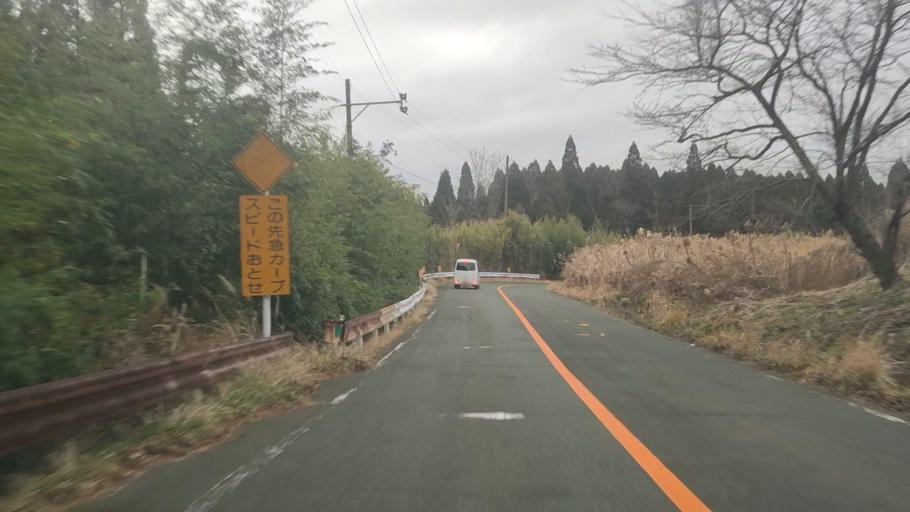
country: JP
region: Kumamoto
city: Aso
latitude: 32.9110
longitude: 131.1318
